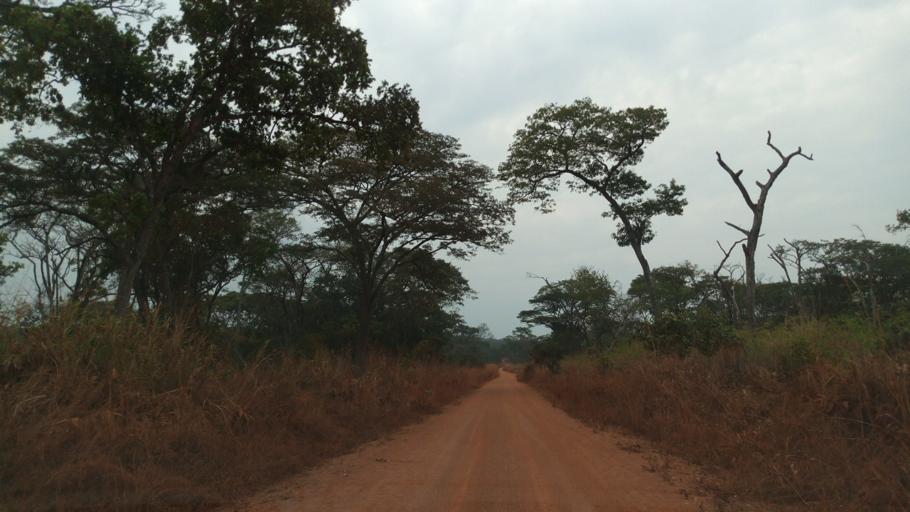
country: ZM
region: Northern
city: Kaputa
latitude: -8.1432
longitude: 29.1099
